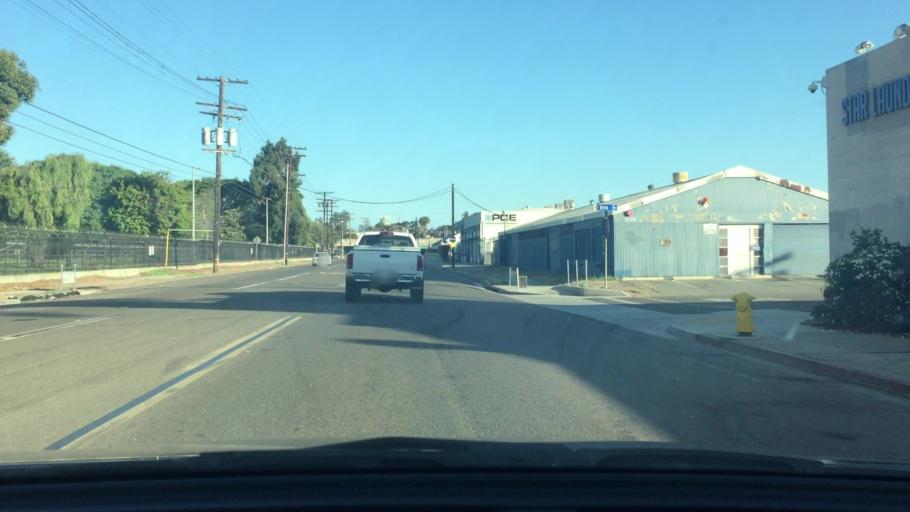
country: US
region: California
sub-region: San Diego County
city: National City
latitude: 32.6889
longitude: -117.1202
